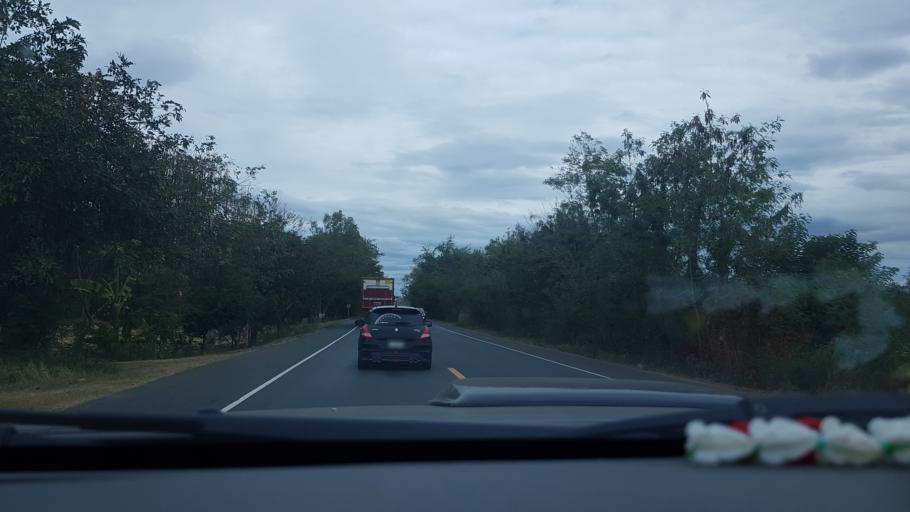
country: TH
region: Phetchabun
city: Phetchabun
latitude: 16.4822
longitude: 101.1357
